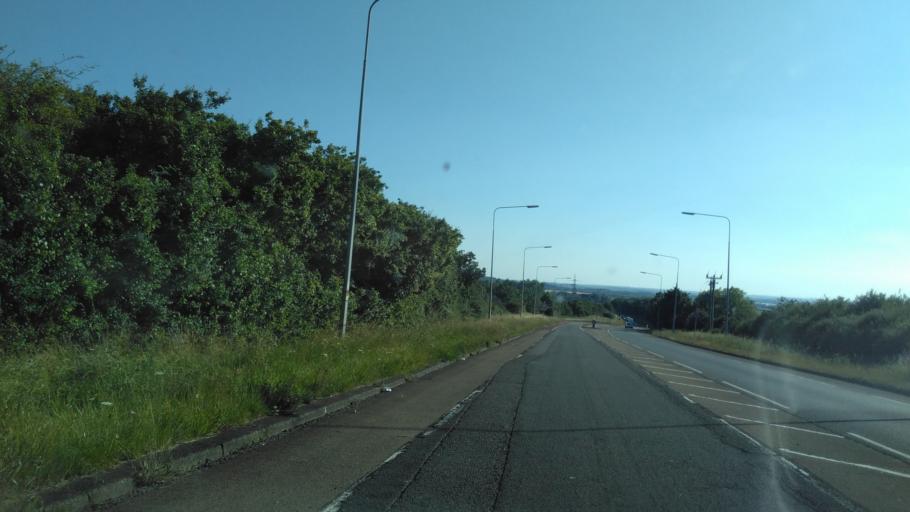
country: GB
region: England
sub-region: Kent
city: Whitstable
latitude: 51.3410
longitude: 1.0105
